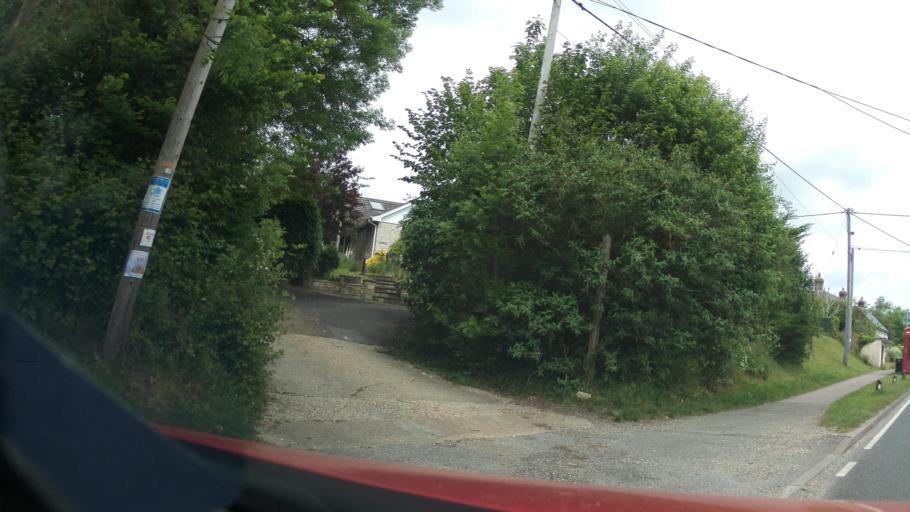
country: GB
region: England
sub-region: Dorset
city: Dorchester
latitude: 50.7329
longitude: -2.4581
